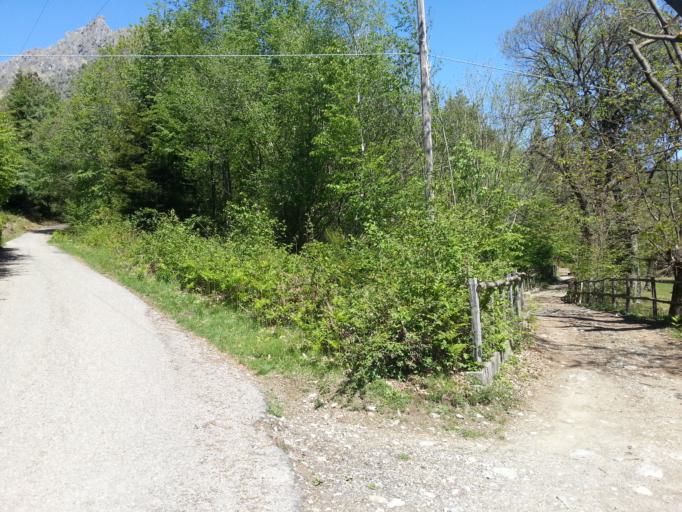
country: IT
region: Lombardy
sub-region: Provincia di Como
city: Plesio
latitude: 46.0460
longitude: 9.2204
